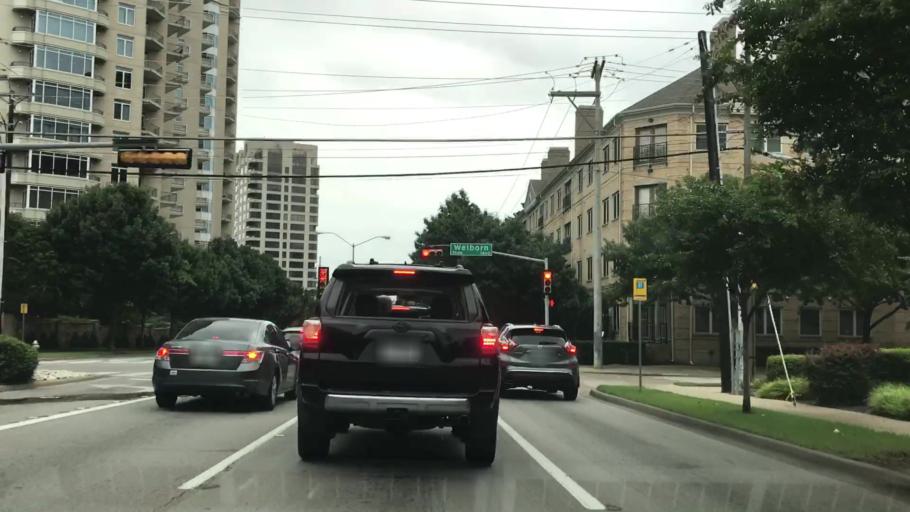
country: US
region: Texas
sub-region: Dallas County
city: Highland Park
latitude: 32.8112
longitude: -96.8049
